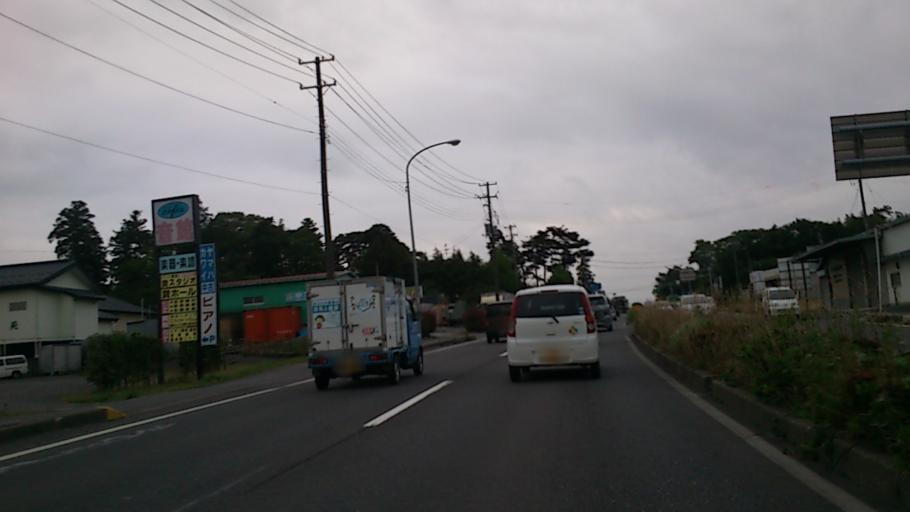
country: JP
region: Fukushima
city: Sukagawa
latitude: 37.2858
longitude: 140.3684
